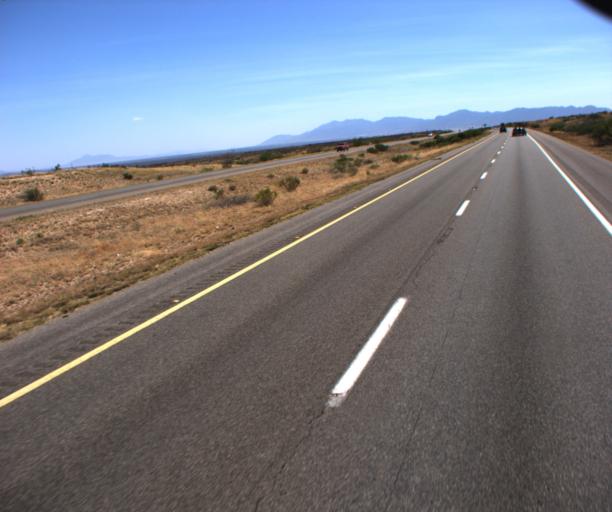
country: US
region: Arizona
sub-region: Cochise County
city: Whetstone
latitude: 31.8095
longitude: -110.3490
